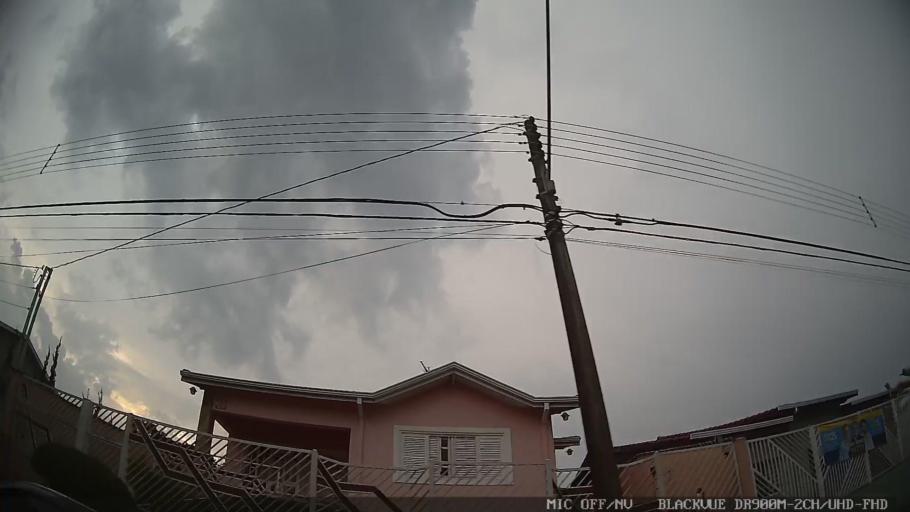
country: BR
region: Sao Paulo
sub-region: Braganca Paulista
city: Braganca Paulista
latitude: -22.9614
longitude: -46.5448
